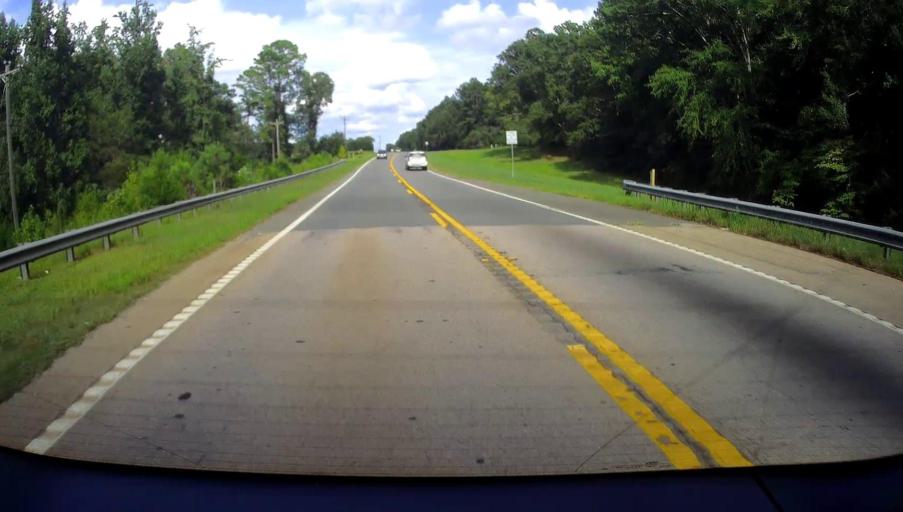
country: US
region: Georgia
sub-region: Meriwether County
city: Manchester
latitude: 32.9899
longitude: -84.5276
